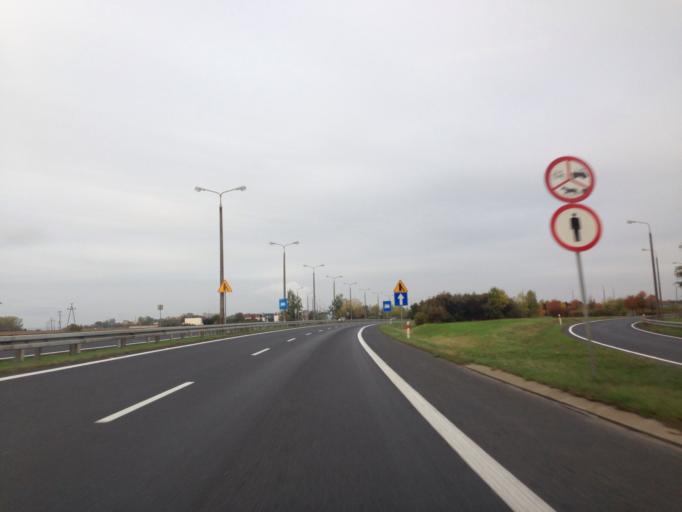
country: PL
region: Kujawsko-Pomorskie
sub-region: Powiat swiecki
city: Swiecie
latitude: 53.4205
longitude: 18.4865
